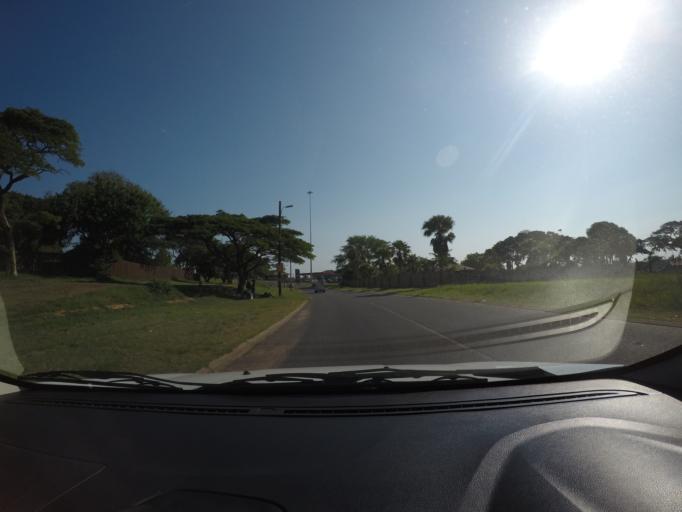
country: ZA
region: KwaZulu-Natal
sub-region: uThungulu District Municipality
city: Richards Bay
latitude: -28.7211
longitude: 32.0415
